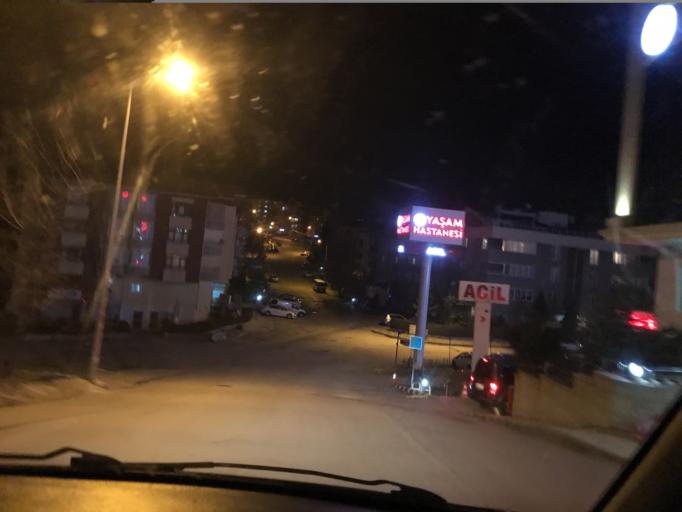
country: TR
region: Ankara
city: Cankaya
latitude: 39.8831
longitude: 32.8715
